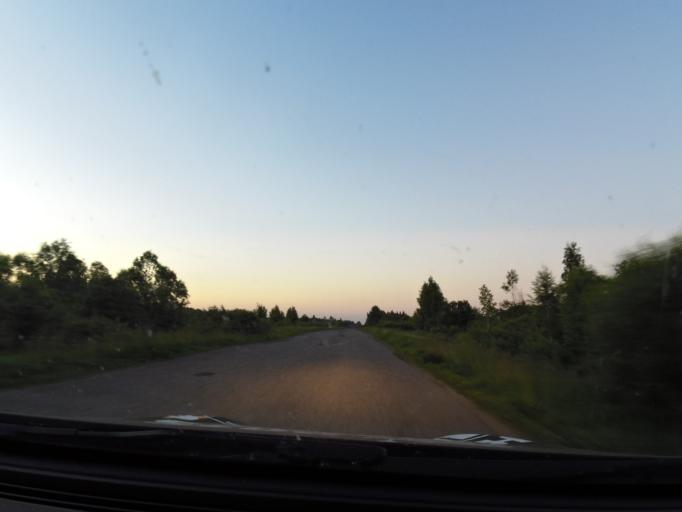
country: RU
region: Kostroma
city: Buy
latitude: 58.4720
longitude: 41.4256
